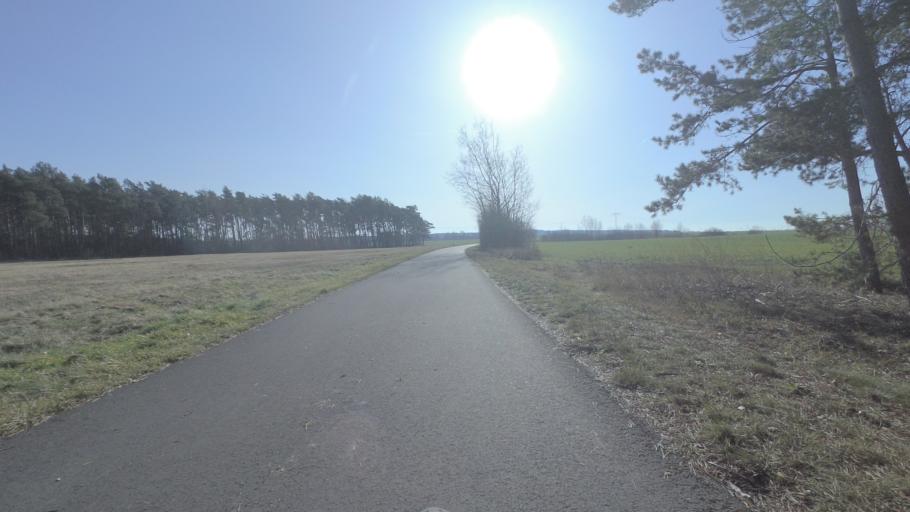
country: DE
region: Brandenburg
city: Luckenwalde
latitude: 52.0477
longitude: 13.1338
